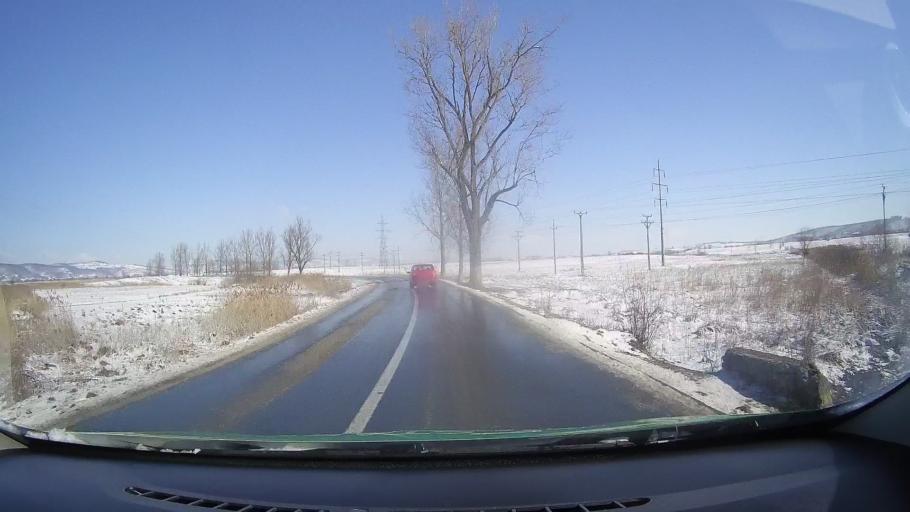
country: RO
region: Sibiu
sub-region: Comuna Avrig
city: Marsa
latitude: 45.7062
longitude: 24.3685
